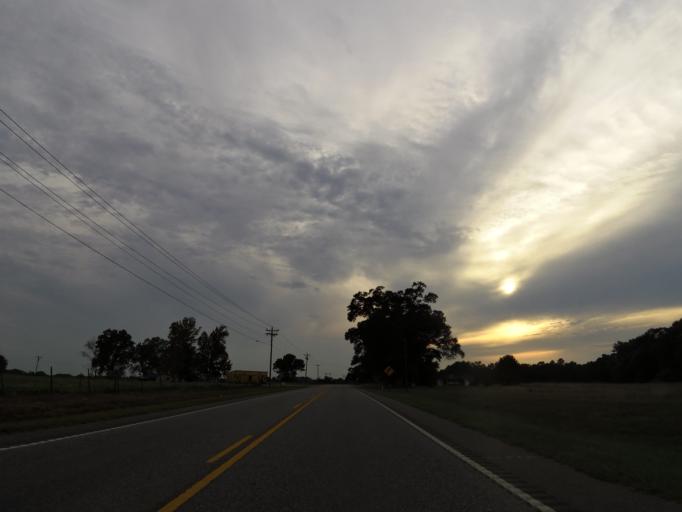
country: US
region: Alabama
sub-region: Escambia County
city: Atmore
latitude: 31.0098
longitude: -87.5666
